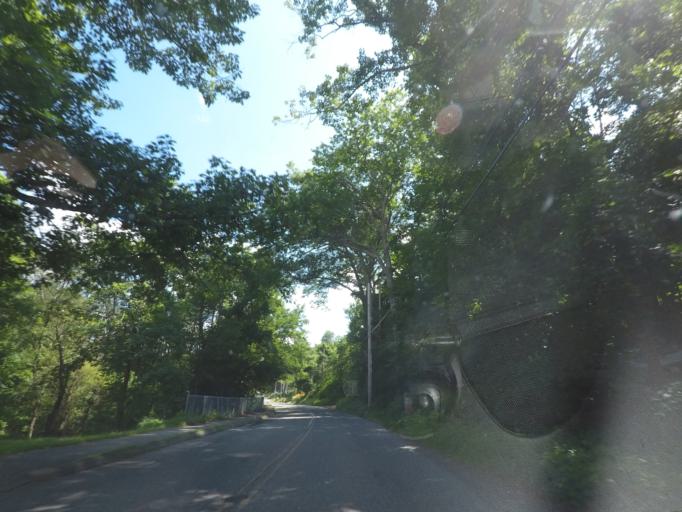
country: US
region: Massachusetts
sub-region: Hampden County
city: Palmer
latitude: 42.1537
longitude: -72.3324
